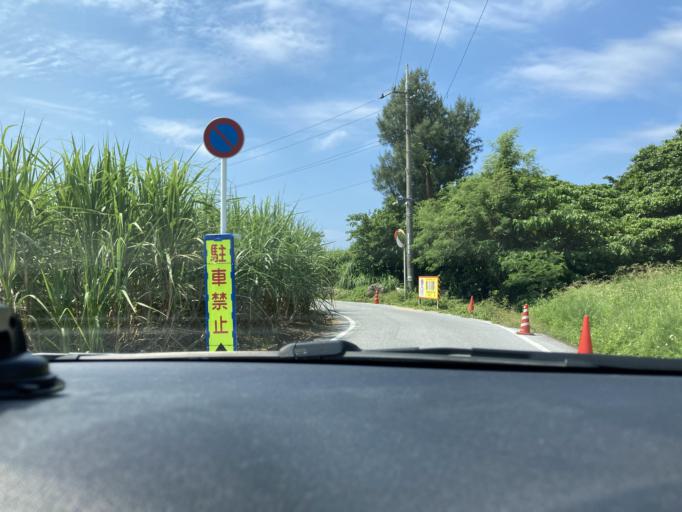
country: JP
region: Okinawa
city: Ishikawa
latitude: 26.4429
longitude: 127.7708
